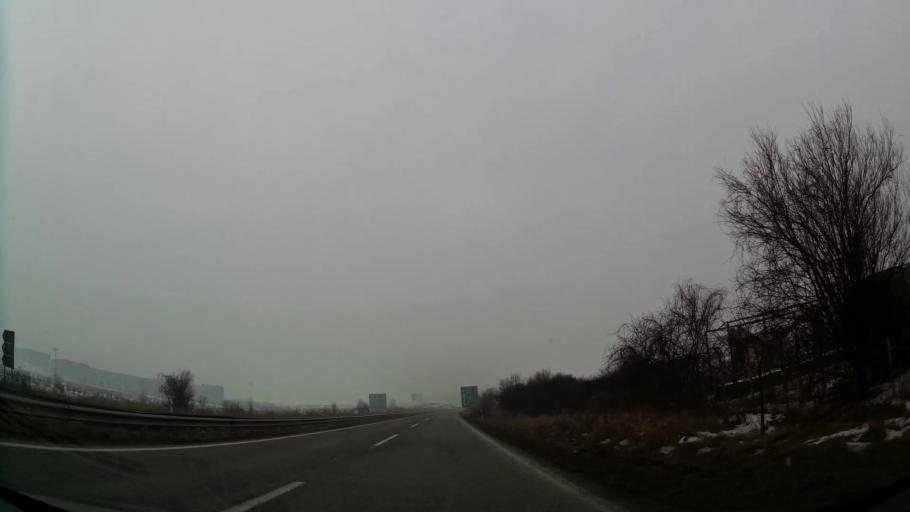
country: MK
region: Petrovec
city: Petrovec
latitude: 41.9497
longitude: 21.6308
